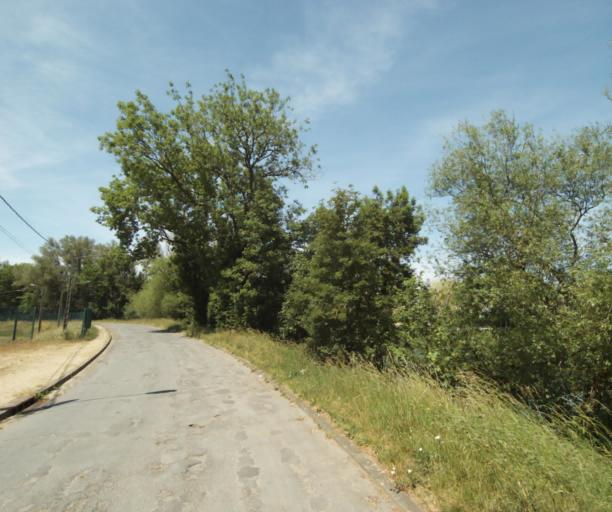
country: FR
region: Champagne-Ardenne
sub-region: Departement des Ardennes
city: Charleville-Mezieres
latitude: 49.7644
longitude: 4.7166
